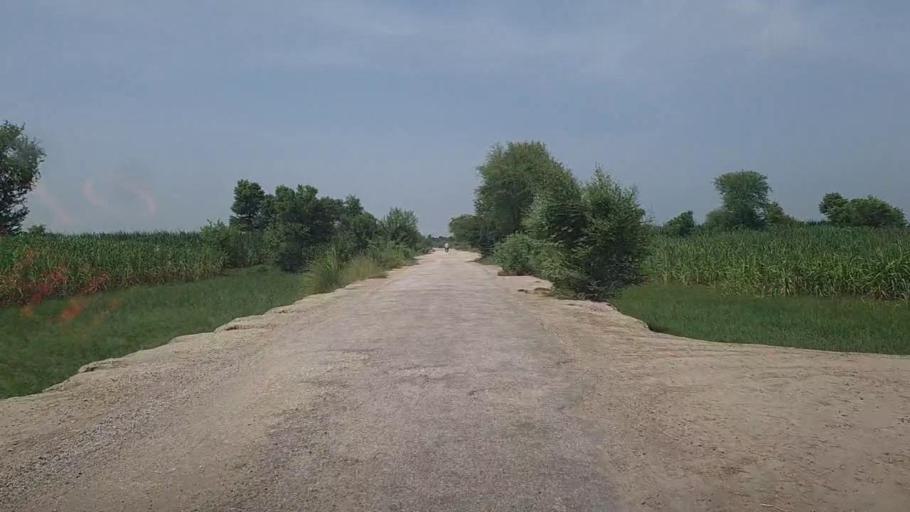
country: PK
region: Sindh
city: Ubauro
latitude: 28.1809
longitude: 69.7695
